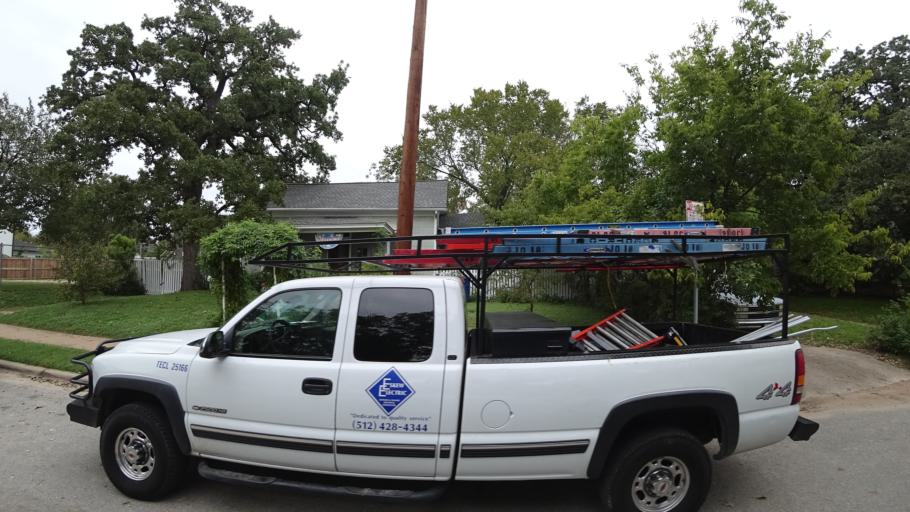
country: US
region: Texas
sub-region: Travis County
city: Austin
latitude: 30.2745
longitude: -97.7289
